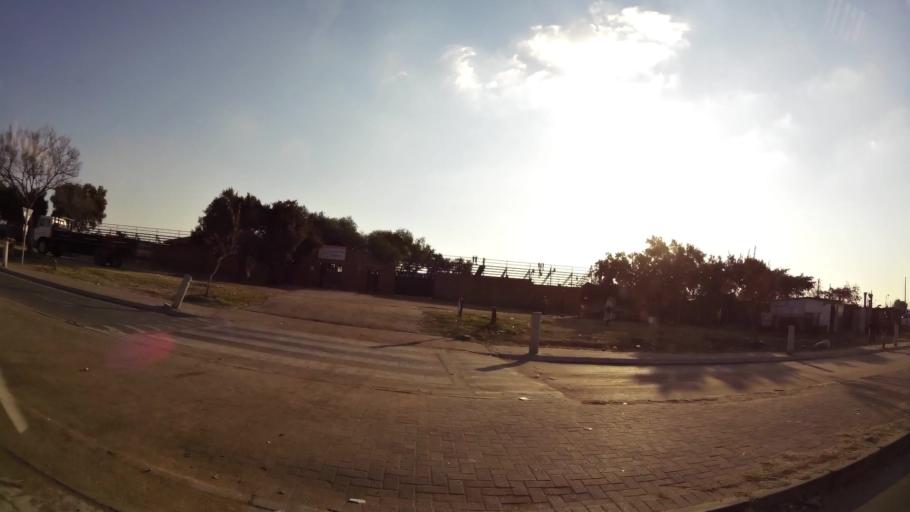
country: ZA
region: Gauteng
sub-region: Ekurhuleni Metropolitan Municipality
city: Tembisa
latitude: -26.0072
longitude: 28.1899
